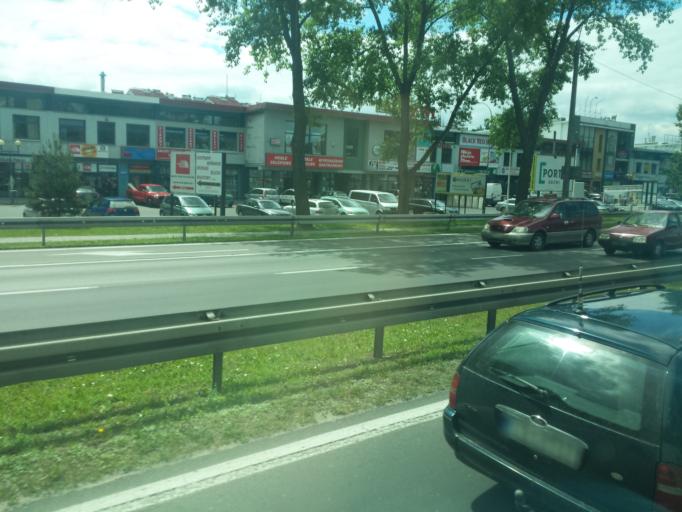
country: PL
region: Masovian Voivodeship
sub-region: Warszawa
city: Wesola
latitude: 52.2235
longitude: 21.2330
